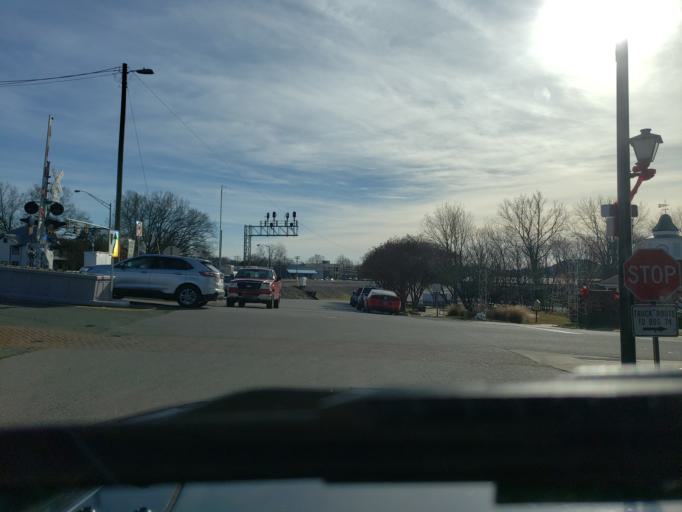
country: US
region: North Carolina
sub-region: Cleveland County
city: Kings Mountain
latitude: 35.2382
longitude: -81.3449
